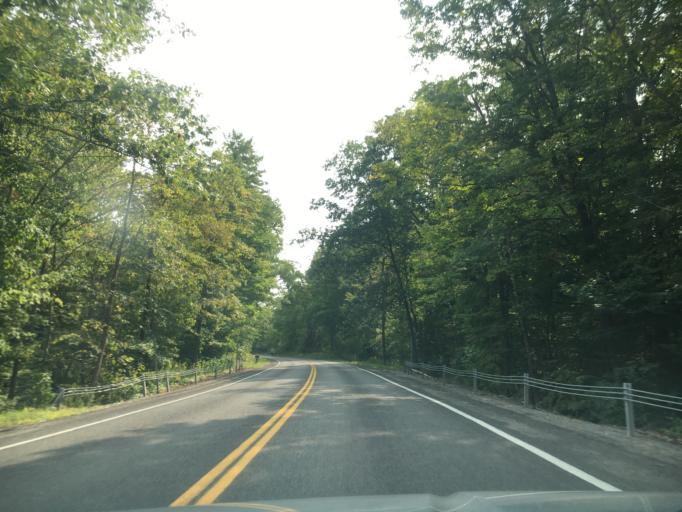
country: US
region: New York
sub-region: Steuben County
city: Sylvan Beach
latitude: 42.4849
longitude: -77.1266
